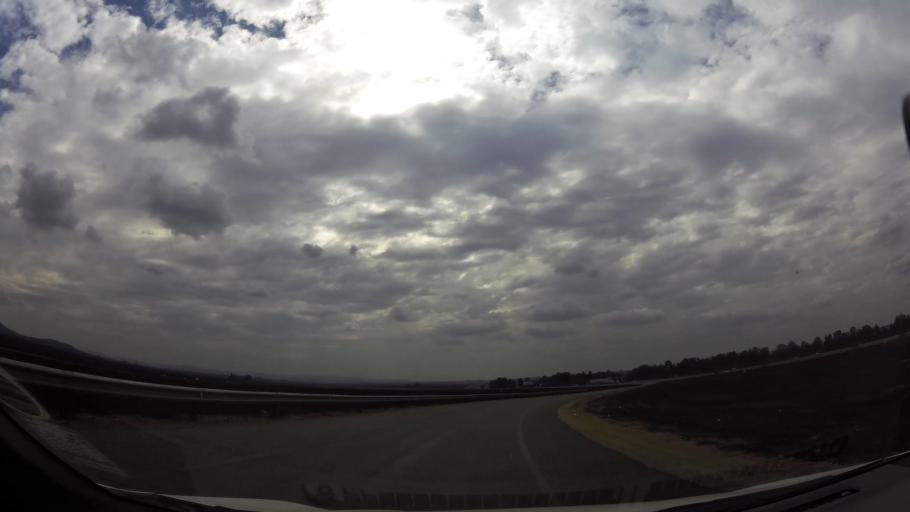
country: ZA
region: Gauteng
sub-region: Sedibeng District Municipality
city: Meyerton
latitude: -26.4162
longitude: 28.0753
